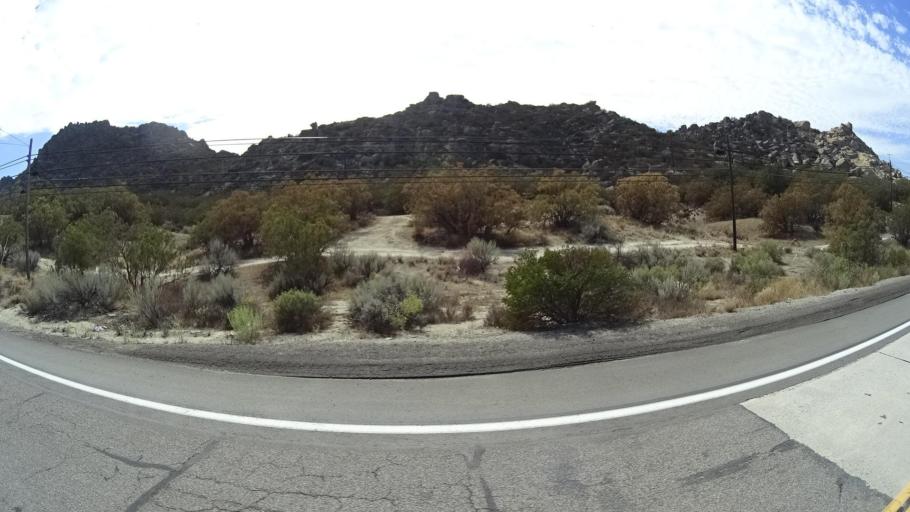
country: MX
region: Baja California
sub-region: Tecate
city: Cereso del Hongo
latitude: 32.6564
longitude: -116.2477
